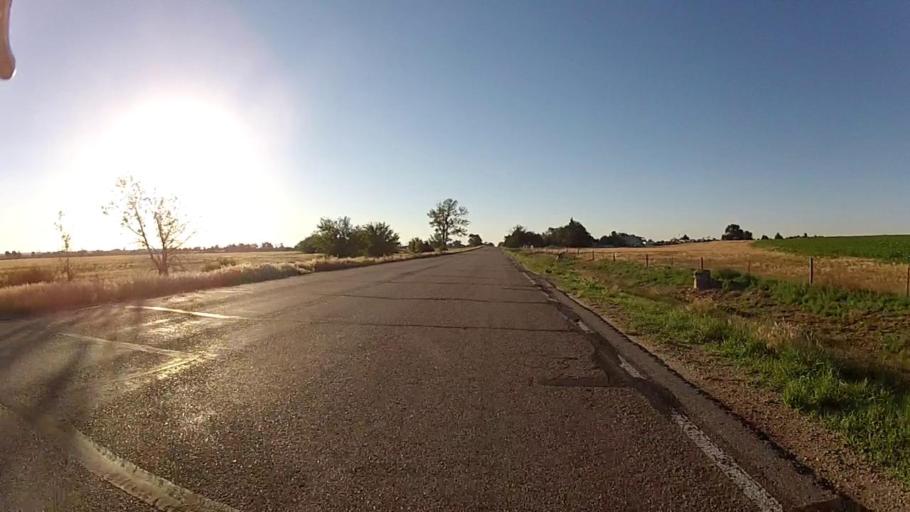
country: US
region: Kansas
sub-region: Ford County
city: Dodge City
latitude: 37.7174
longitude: -99.9401
